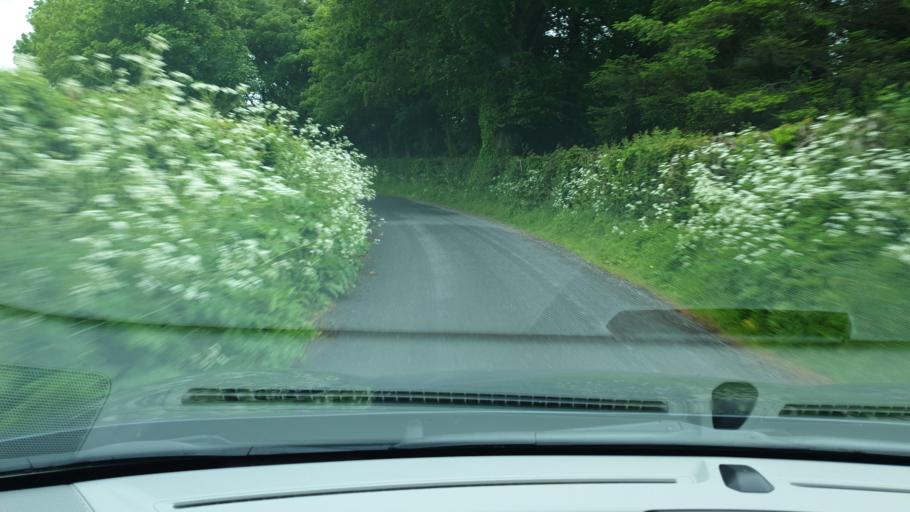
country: IE
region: Leinster
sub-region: Laois
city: Portlaoise
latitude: 53.0361
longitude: -7.3374
